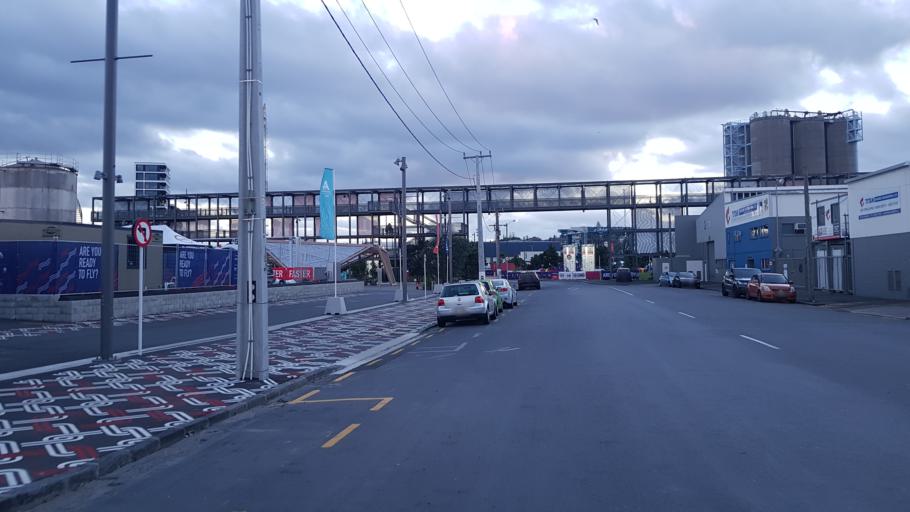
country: NZ
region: Auckland
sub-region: Auckland
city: Auckland
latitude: -36.8390
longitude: 174.7558
